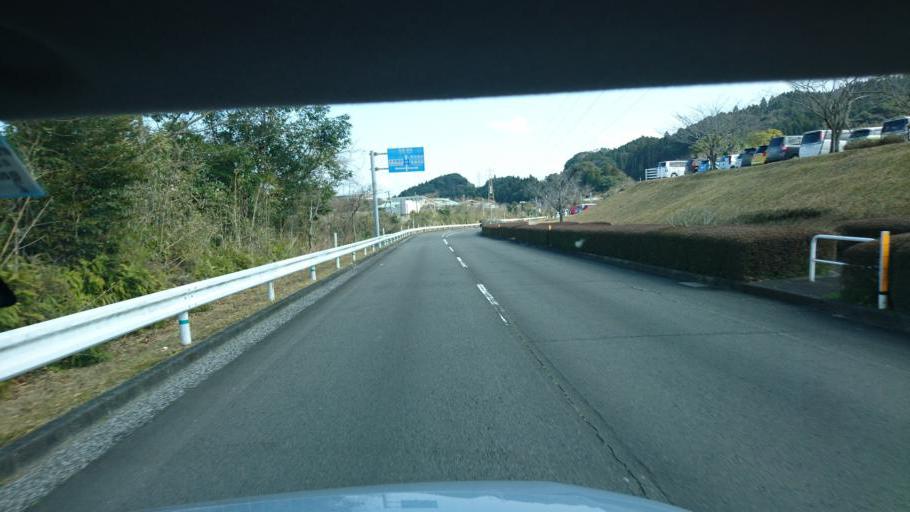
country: JP
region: Miyazaki
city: Miyazaki-shi
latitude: 31.8364
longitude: 131.3999
